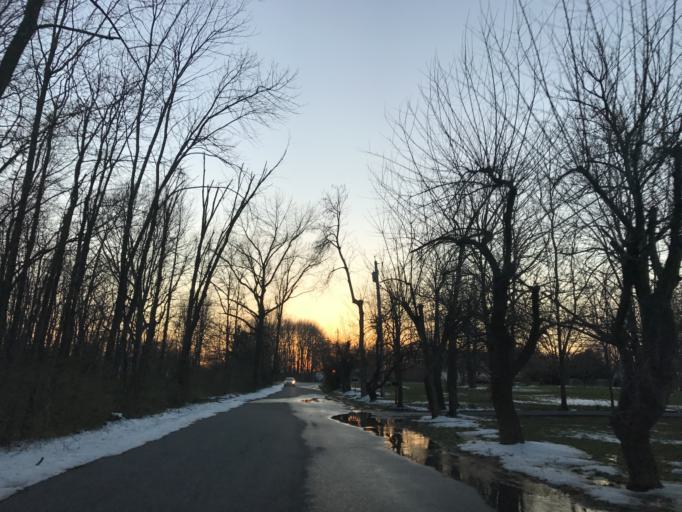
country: US
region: Maryland
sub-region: Baltimore County
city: Middle River
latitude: 39.3026
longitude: -76.4370
